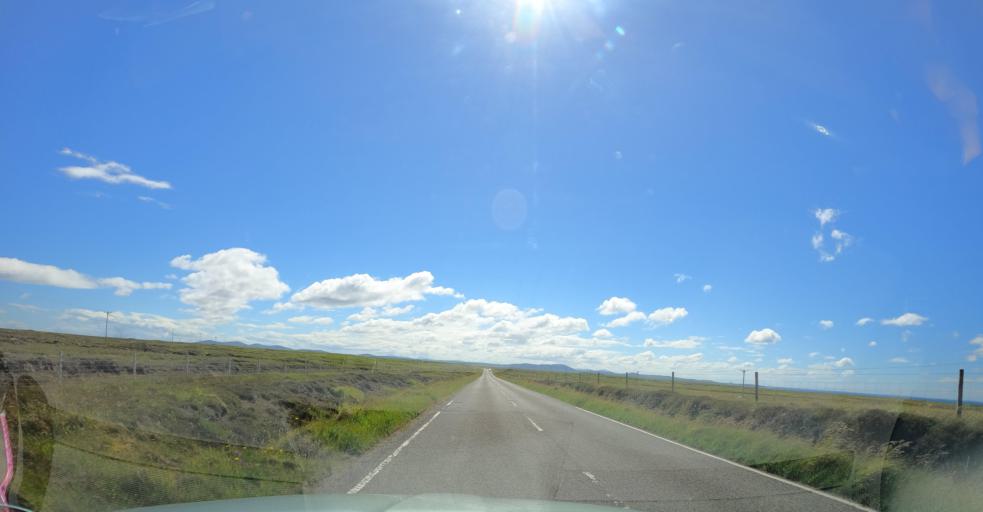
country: GB
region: Scotland
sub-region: Eilean Siar
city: Isle of Lewis
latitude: 58.3816
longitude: -6.5029
